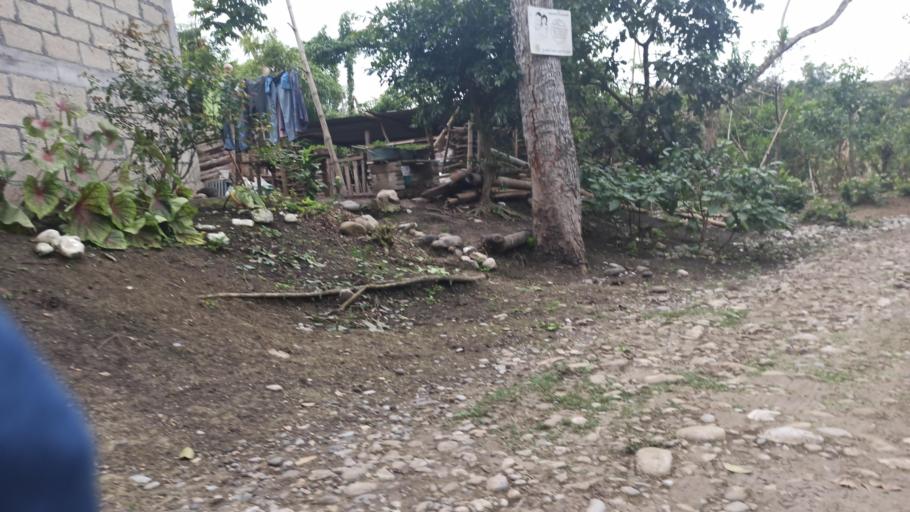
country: MX
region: Veracruz
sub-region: Papantla
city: El Chote
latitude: 20.3655
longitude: -97.4303
